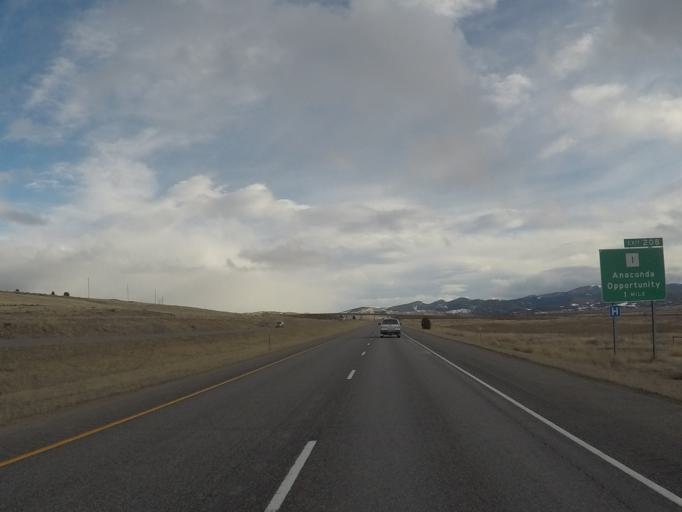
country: US
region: Montana
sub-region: Deer Lodge County
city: Warm Springs
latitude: 46.1133
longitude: -112.7991
